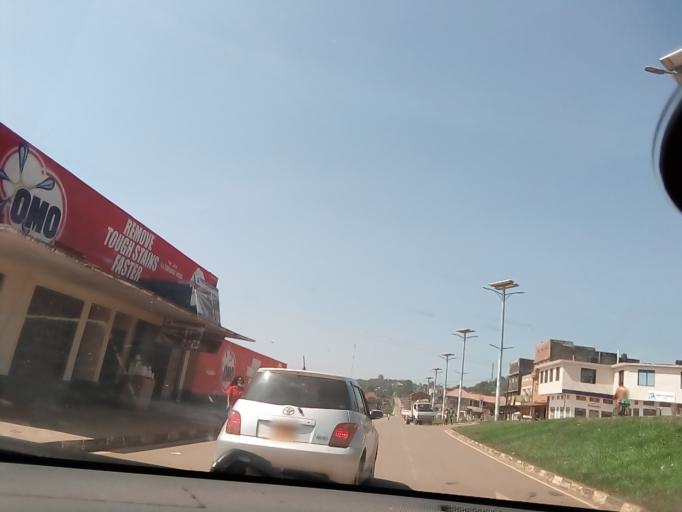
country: UG
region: Central Region
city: Masaka
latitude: -0.3444
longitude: 31.7403
